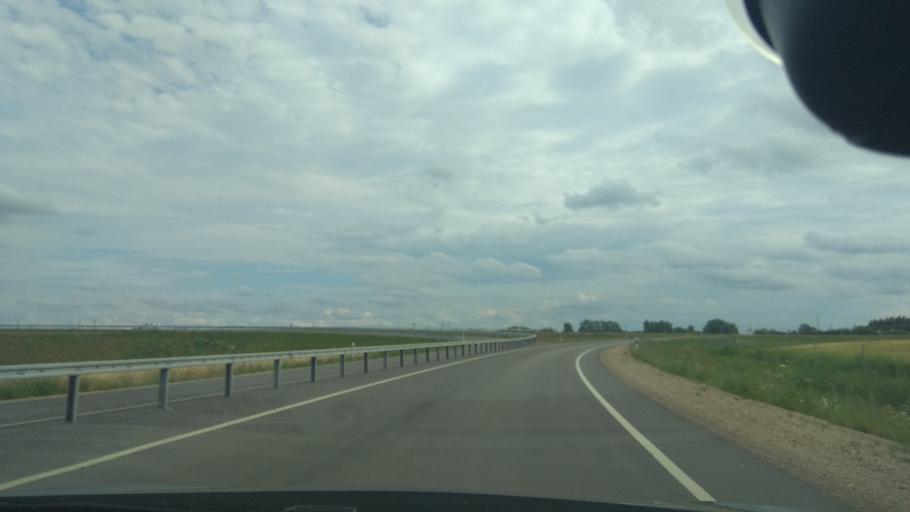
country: LT
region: Panevezys
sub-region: Panevezys City
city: Panevezys
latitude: 55.7324
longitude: 24.2731
